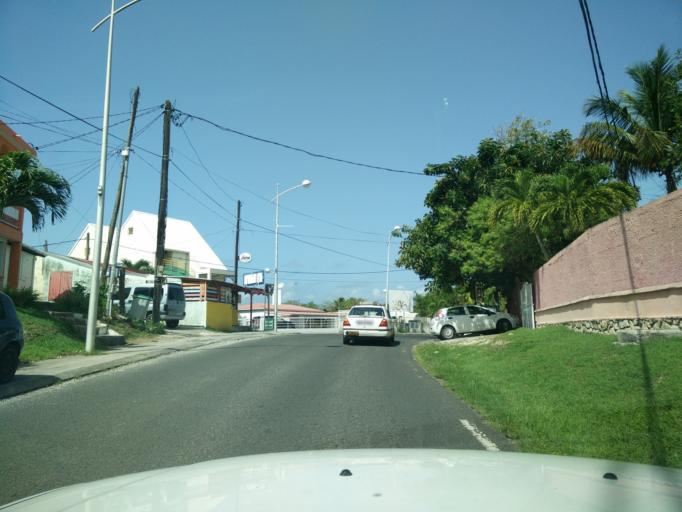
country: GP
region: Guadeloupe
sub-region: Guadeloupe
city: Le Gosier
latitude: 16.2065
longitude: -61.4819
